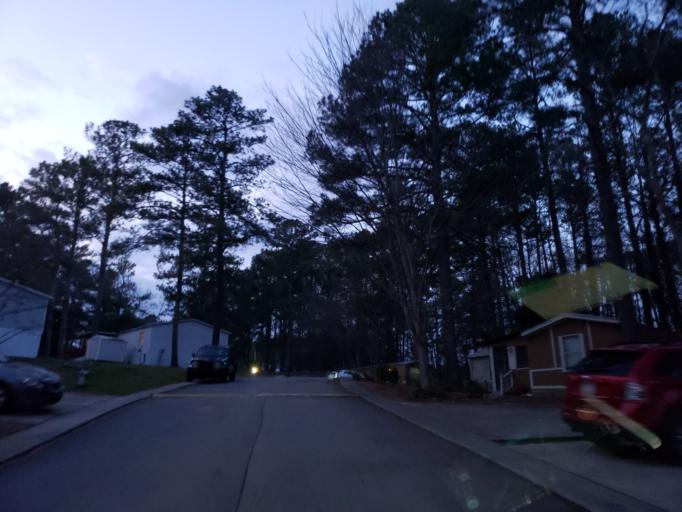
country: US
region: Georgia
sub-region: Cobb County
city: Kennesaw
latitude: 34.0223
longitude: -84.6293
